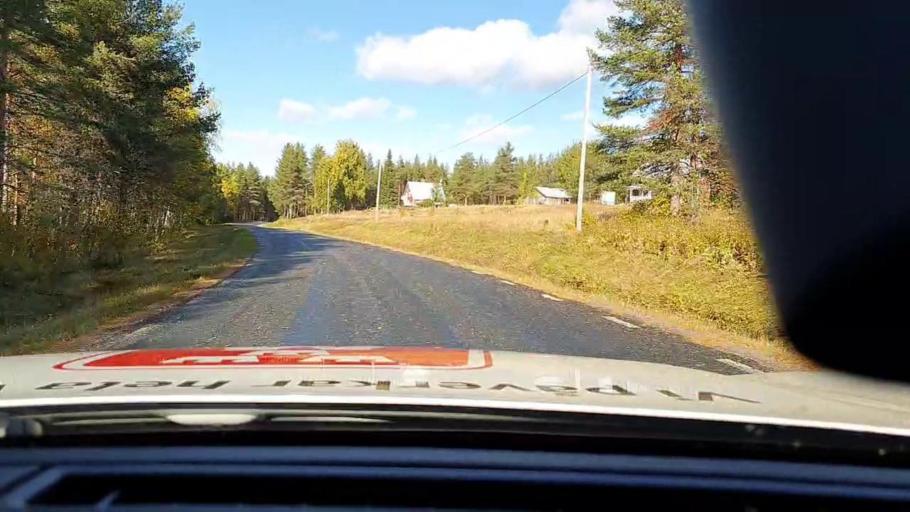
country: SE
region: Vaesterbotten
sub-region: Skelleftea Kommun
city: Langsele
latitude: 65.0141
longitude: 20.0796
